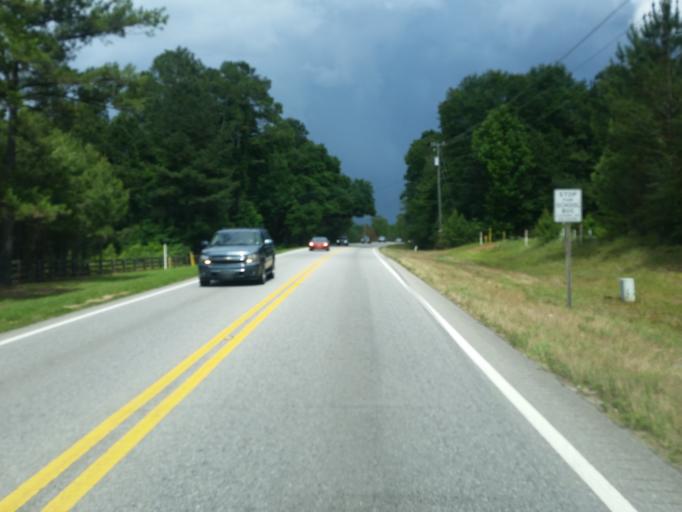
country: US
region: Mississippi
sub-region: Jackson County
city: Hurley
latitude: 30.8259
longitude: -88.3706
